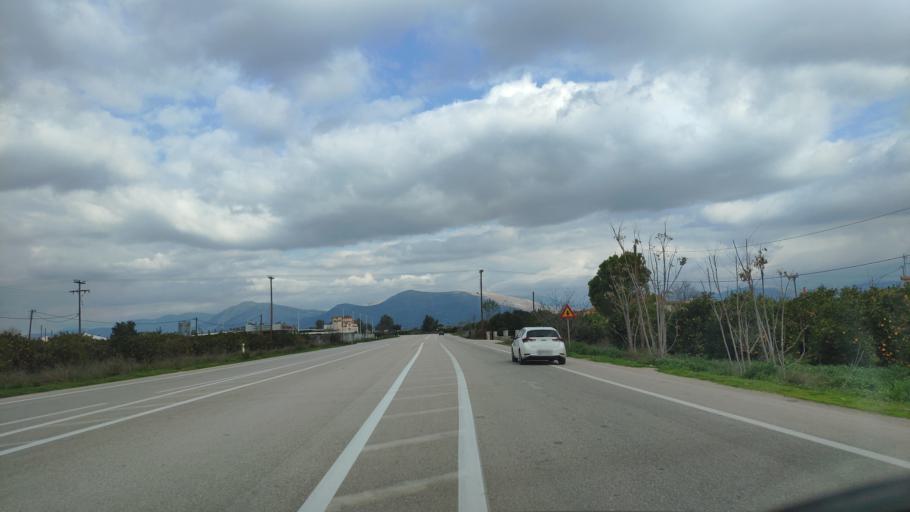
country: GR
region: Peloponnese
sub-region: Nomos Argolidos
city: Argos
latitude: 37.6204
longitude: 22.7348
